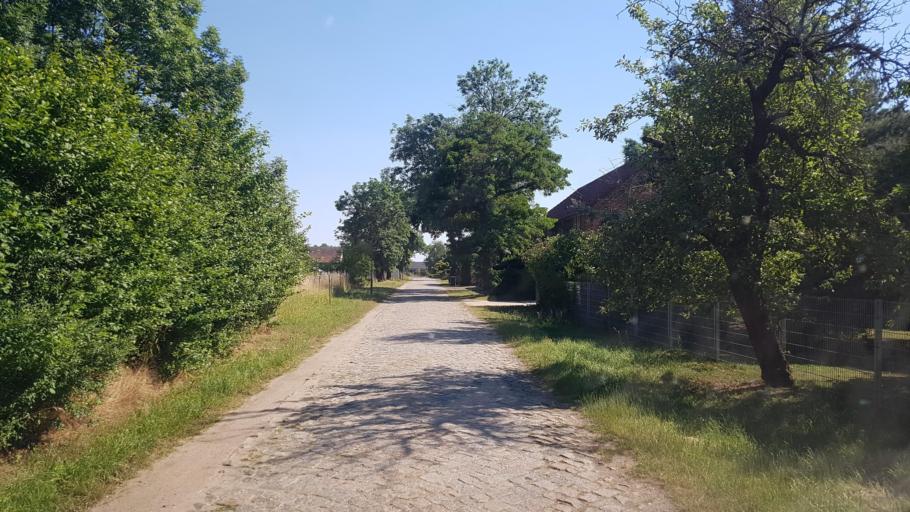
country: DE
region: Saxony-Anhalt
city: Elster
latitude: 51.7726
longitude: 12.8640
